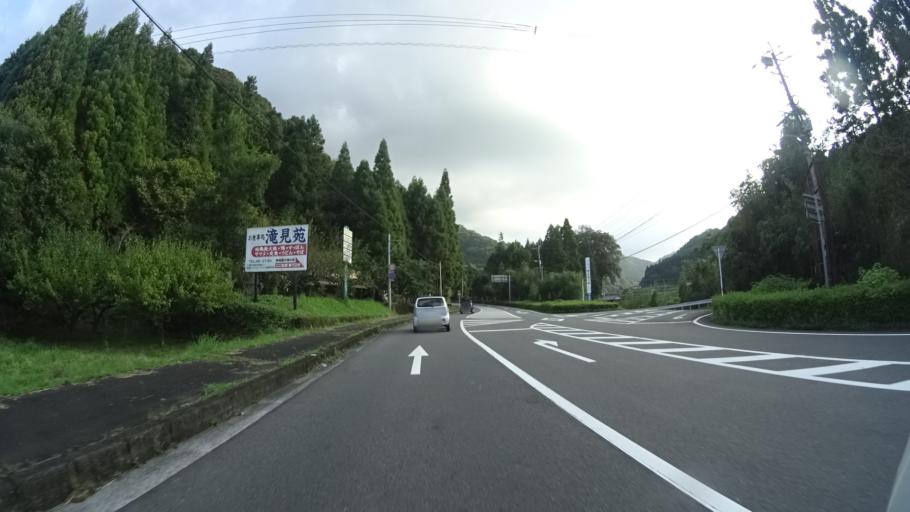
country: JP
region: Oita
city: Hiji
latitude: 33.3716
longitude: 131.3957
